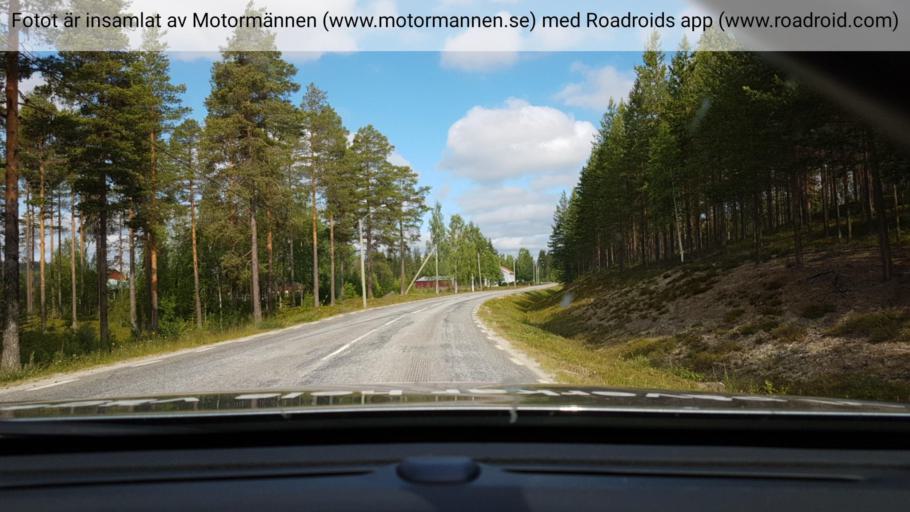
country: SE
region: Vaesterbotten
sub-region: Lycksele Kommun
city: Lycksele
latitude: 64.7652
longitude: 19.0458
